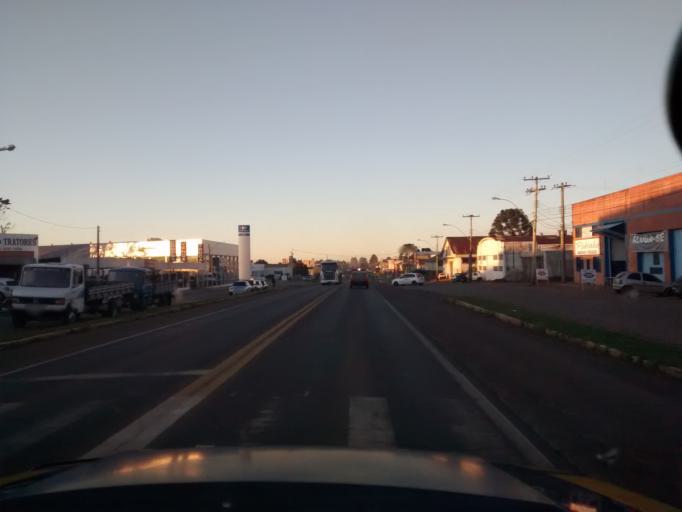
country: BR
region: Rio Grande do Sul
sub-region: Vacaria
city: Vacaria
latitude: -28.5115
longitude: -50.9318
